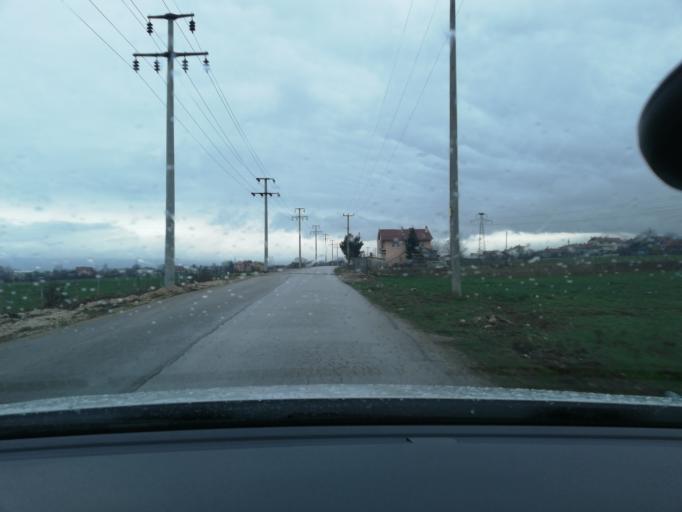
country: TR
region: Bolu
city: Bolu
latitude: 40.7578
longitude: 31.6405
